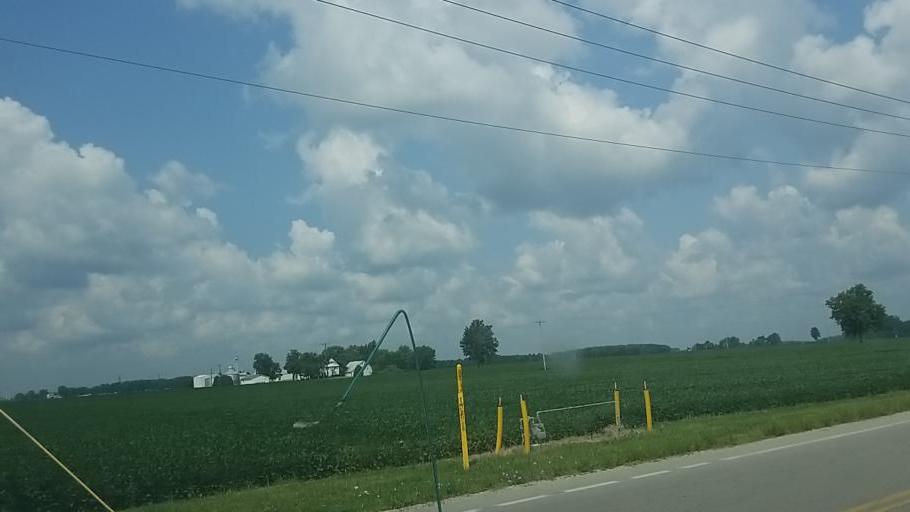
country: US
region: Ohio
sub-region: Wyandot County
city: Upper Sandusky
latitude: 40.8531
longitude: -83.2796
